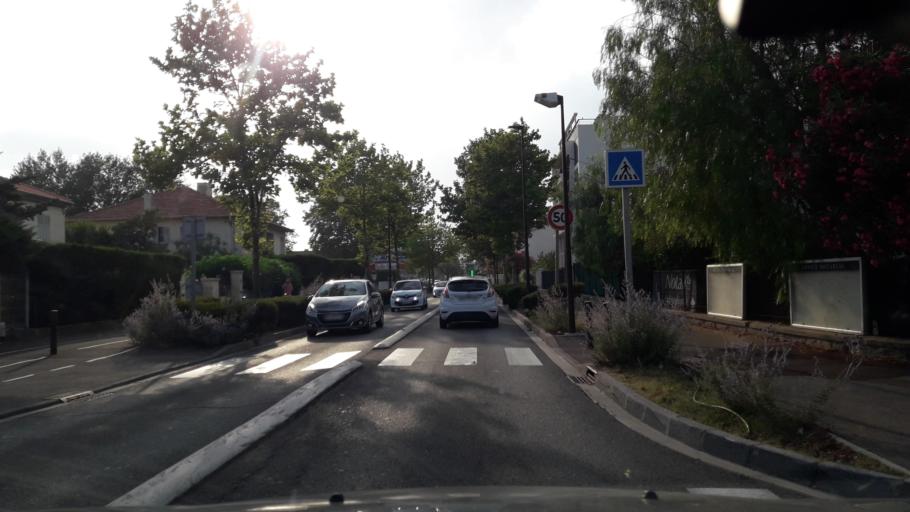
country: FR
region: Provence-Alpes-Cote d'Azur
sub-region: Departement du Var
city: Saint-Raphael
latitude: 43.4295
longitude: 6.7604
